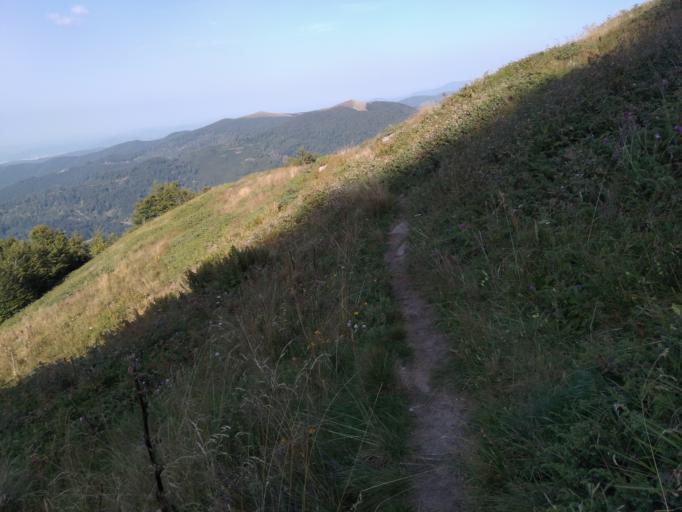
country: BG
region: Stara Zagora
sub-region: Obshtina Pavel Banya
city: Asen
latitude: 42.7618
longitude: 25.1090
